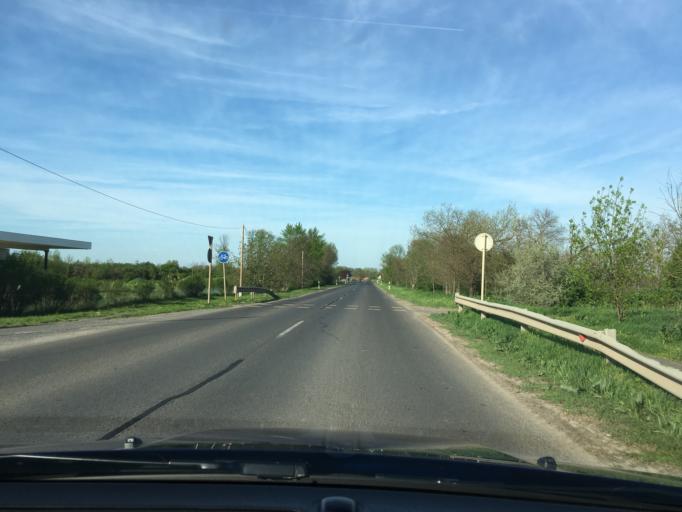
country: HU
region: Bekes
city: Korostarcsa
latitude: 46.8684
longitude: 21.0237
